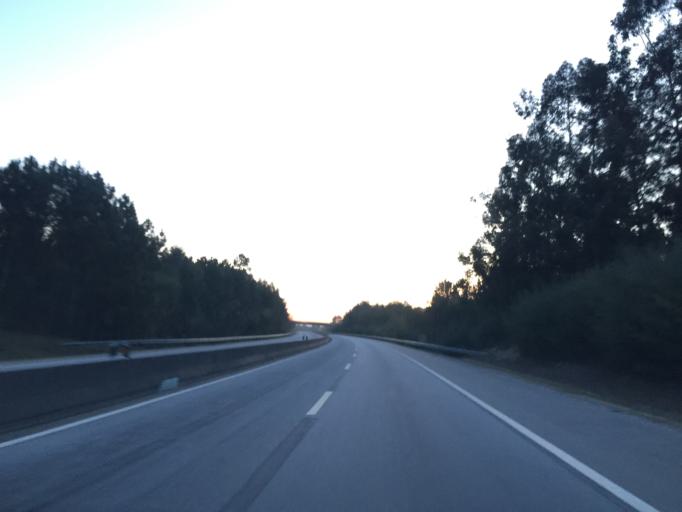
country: PT
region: Coimbra
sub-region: Tabua
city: Tabua
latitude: 40.4101
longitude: -8.0661
